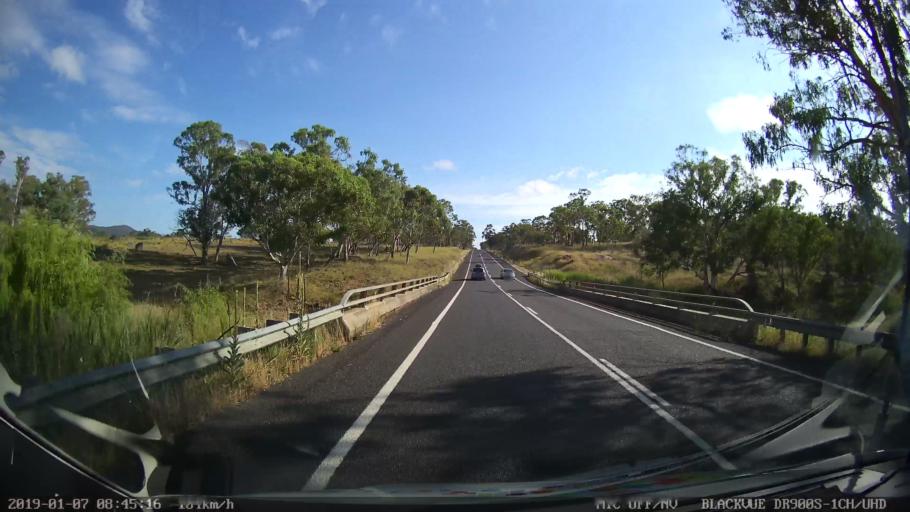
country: AU
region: New South Wales
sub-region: Tamworth Municipality
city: Kootingal
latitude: -30.8215
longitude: 151.2235
